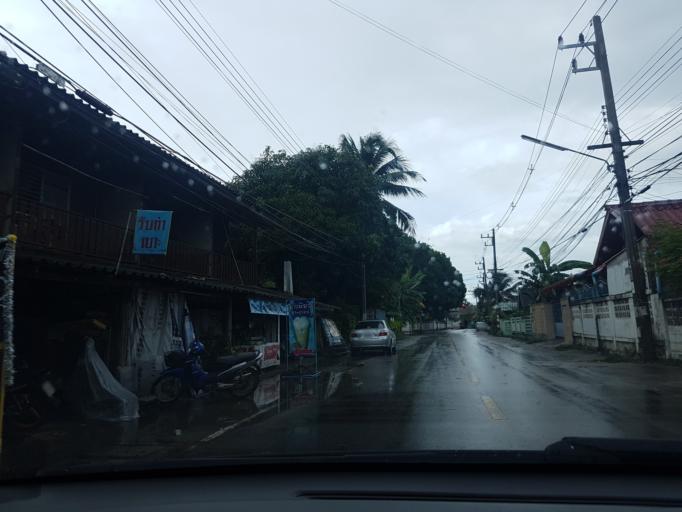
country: TH
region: Lampang
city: Lampang
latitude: 18.2882
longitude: 99.4737
